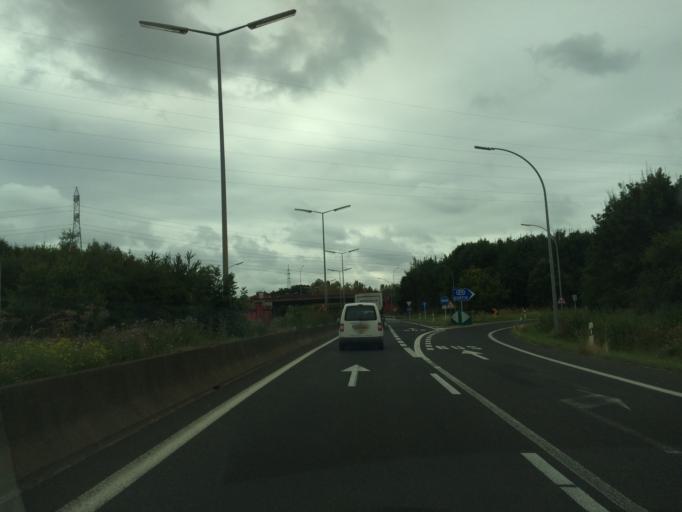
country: LU
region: Luxembourg
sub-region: Canton d'Esch-sur-Alzette
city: Mondercange
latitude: 49.5179
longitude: 5.9728
